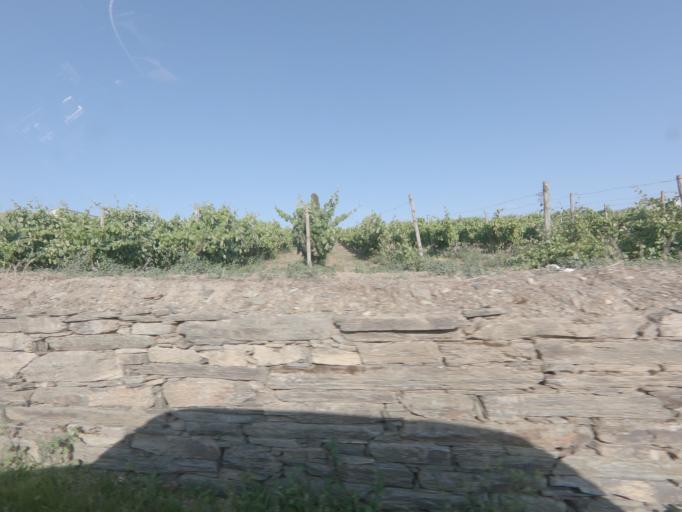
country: PT
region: Vila Real
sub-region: Sabrosa
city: Vilela
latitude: 41.1811
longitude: -7.6061
